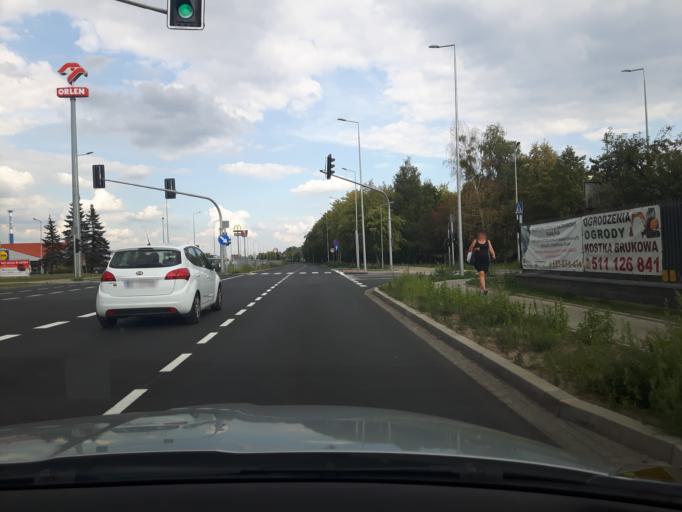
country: PL
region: Masovian Voivodeship
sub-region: Powiat piaseczynski
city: Piaseczno
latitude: 52.0816
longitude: 21.0147
